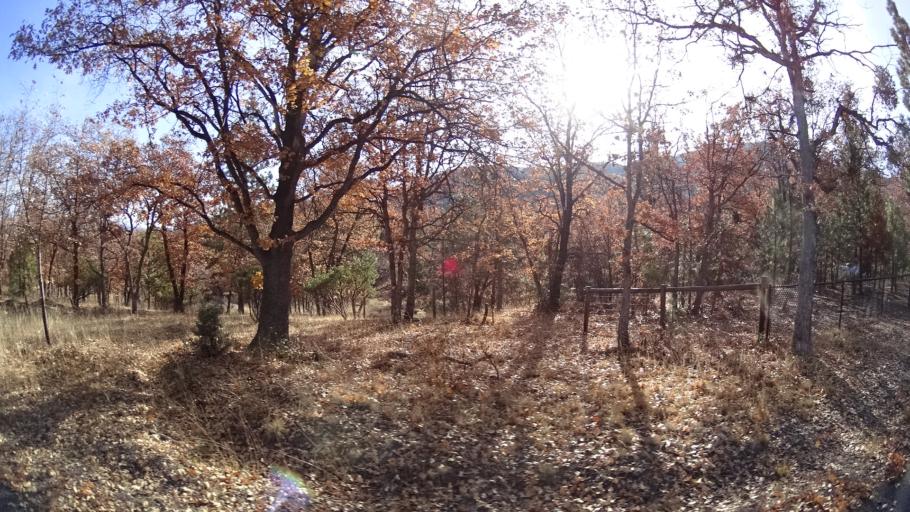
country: US
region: California
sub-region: Siskiyou County
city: Yreka
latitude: 41.6563
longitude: -122.6266
